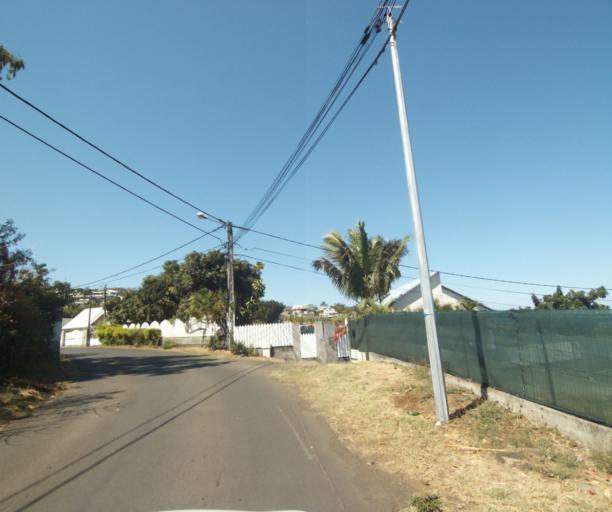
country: RE
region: Reunion
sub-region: Reunion
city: Saint-Paul
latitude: -20.9889
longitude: 55.3238
